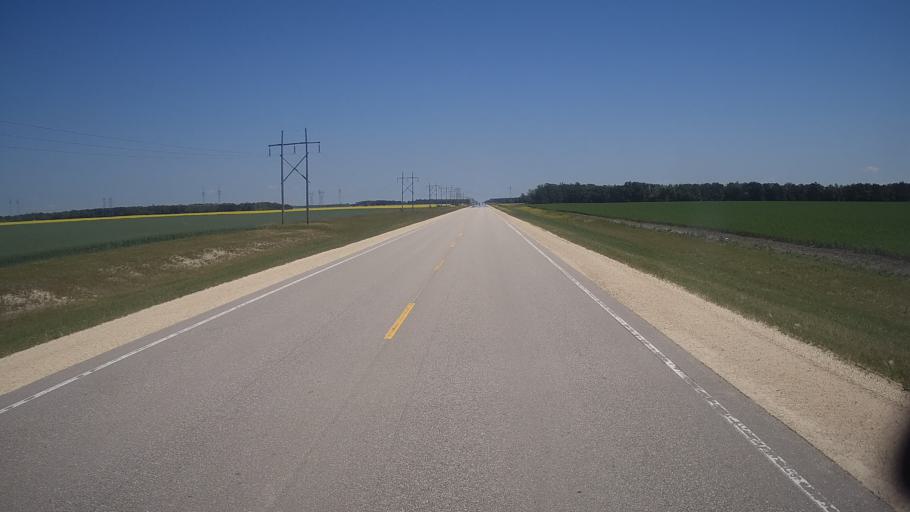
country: CA
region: Manitoba
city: Stonewall
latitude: 50.1227
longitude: -97.5130
